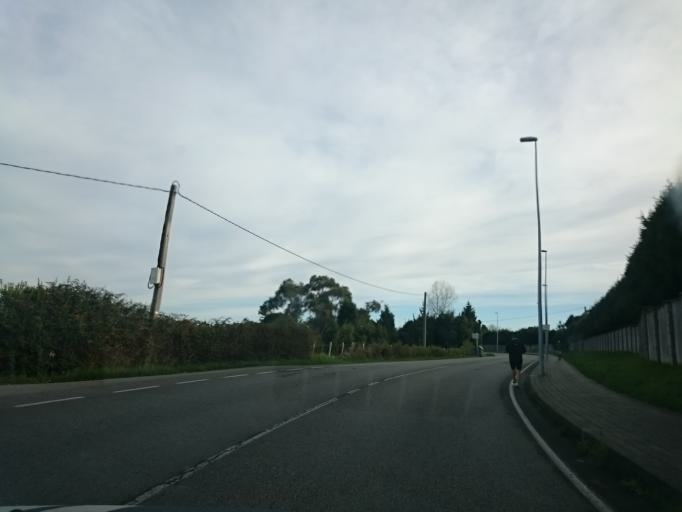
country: ES
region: Asturias
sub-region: Province of Asturias
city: Arriba
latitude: 43.5261
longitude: -5.5904
